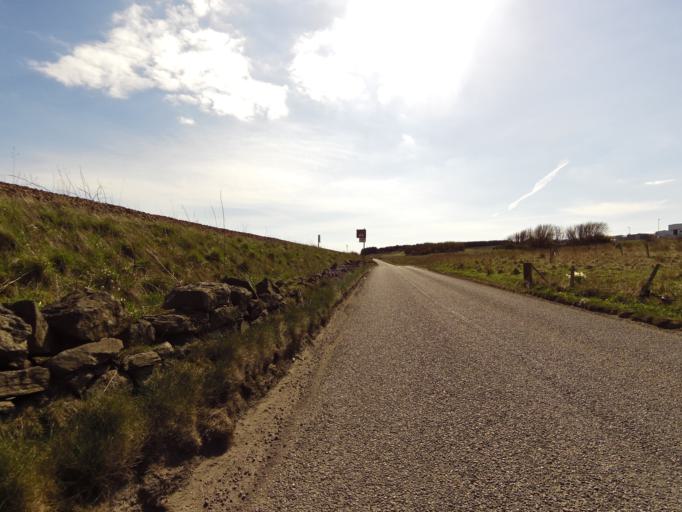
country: GB
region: Scotland
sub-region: Aberdeen City
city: Aberdeen
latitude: 57.1142
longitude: -2.0651
